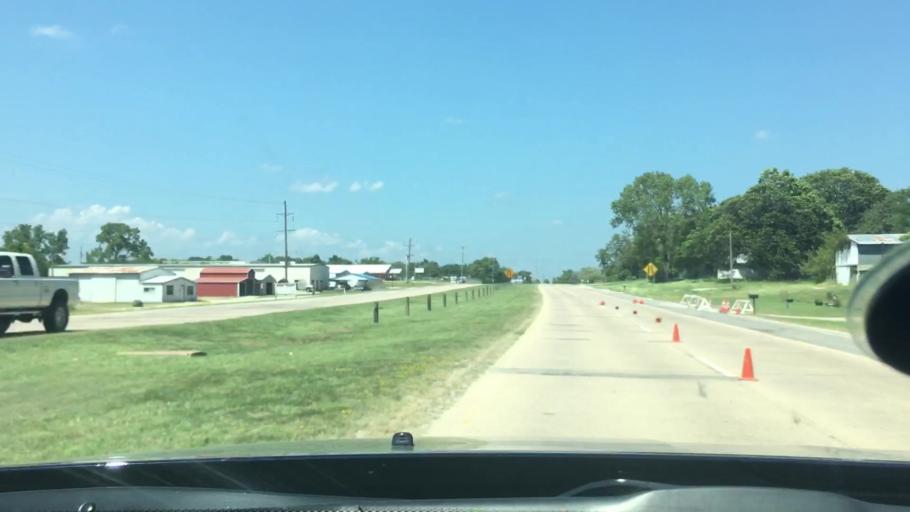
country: US
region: Oklahoma
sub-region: Pontotoc County
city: Ada
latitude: 34.8118
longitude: -96.6783
